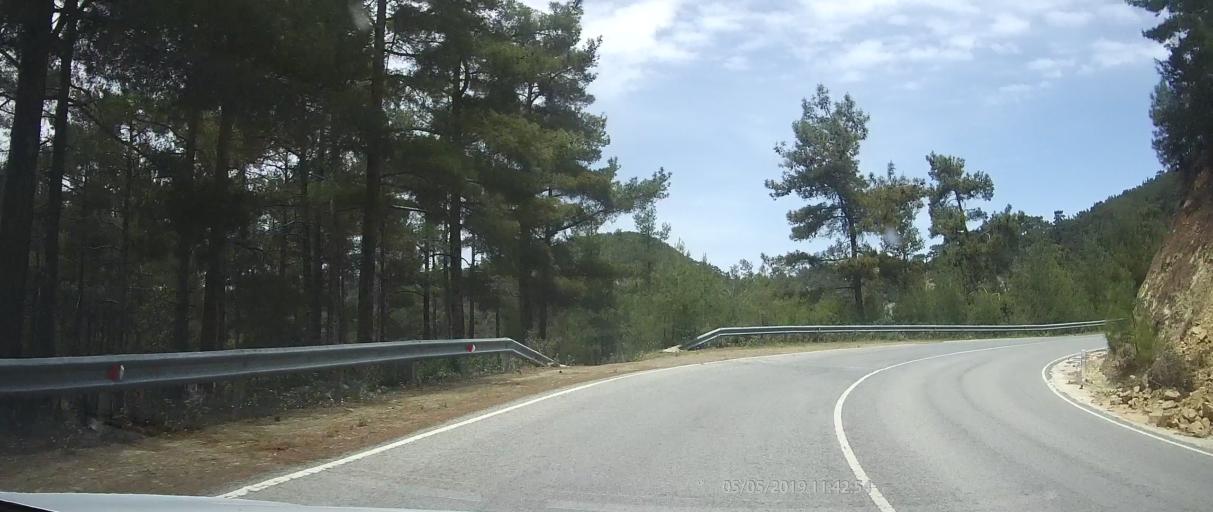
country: CY
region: Lefkosia
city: Kato Pyrgos
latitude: 35.0048
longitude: 32.6703
